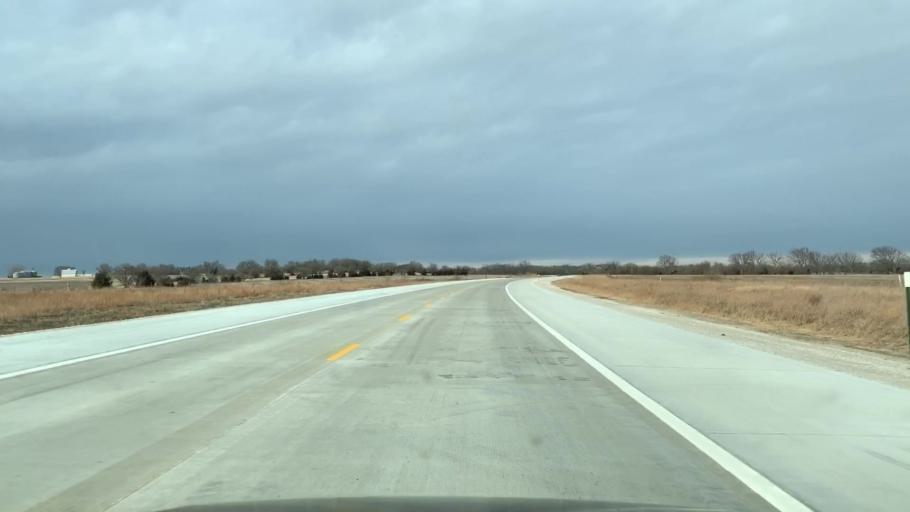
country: US
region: Kansas
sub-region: Allen County
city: Humboldt
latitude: 37.8548
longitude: -95.4087
